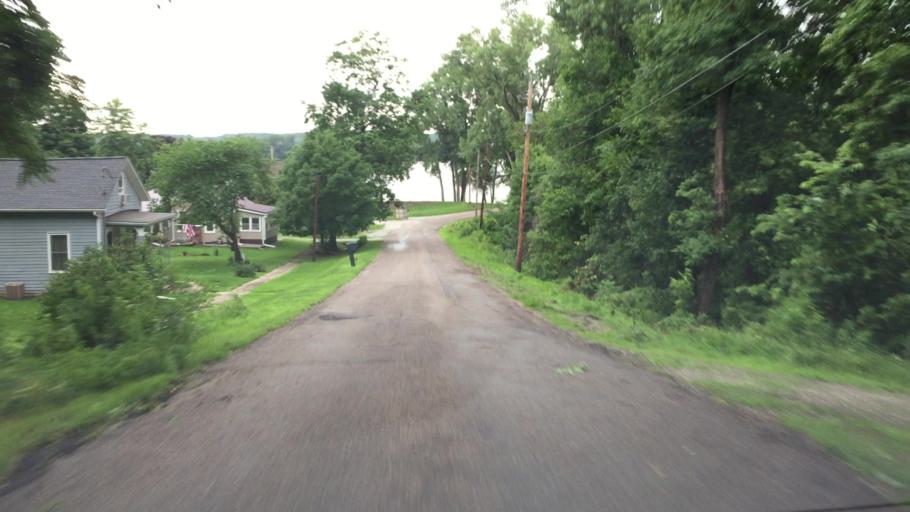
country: US
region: Illinois
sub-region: Hancock County
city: Warsaw
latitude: 40.3643
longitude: -91.4346
